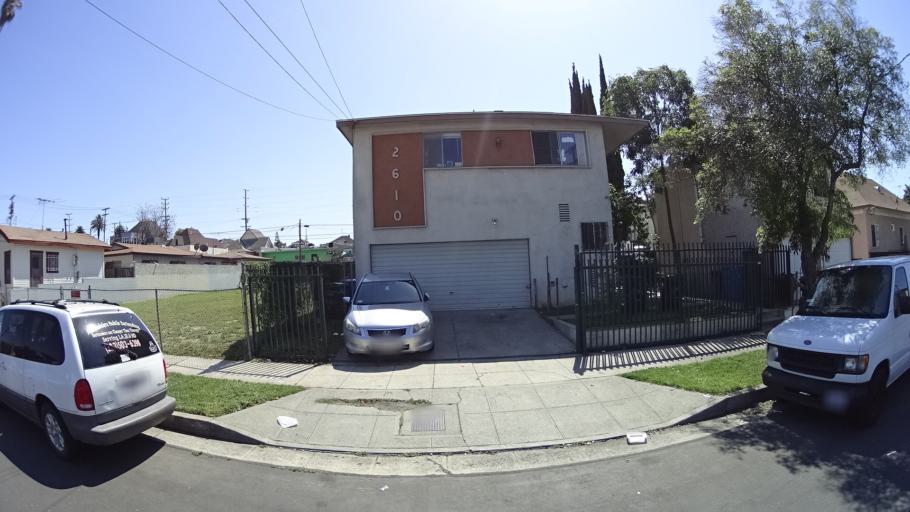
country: US
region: California
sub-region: Los Angeles County
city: Boyle Heights
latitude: 34.0432
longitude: -118.2064
